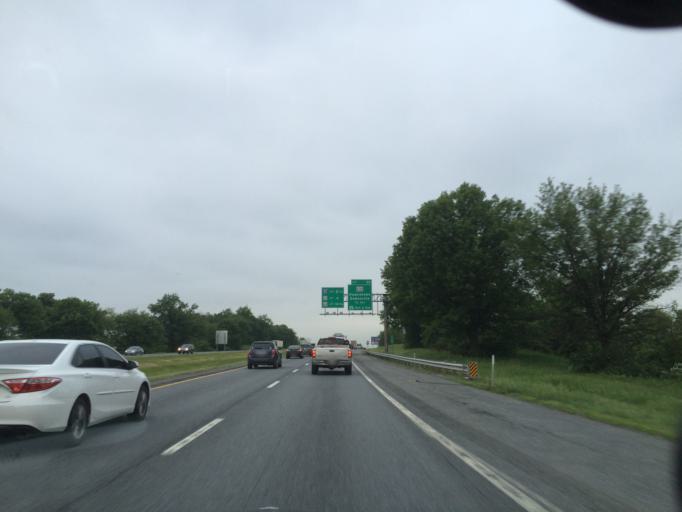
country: US
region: Maryland
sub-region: Washington County
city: Halfway
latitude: 39.6054
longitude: -77.7369
